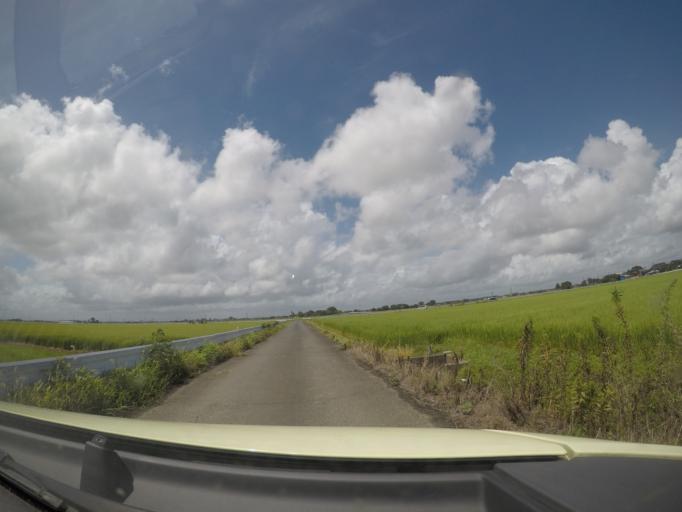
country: JP
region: Ibaraki
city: Mitsukaido
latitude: 36.0583
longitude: 140.0081
